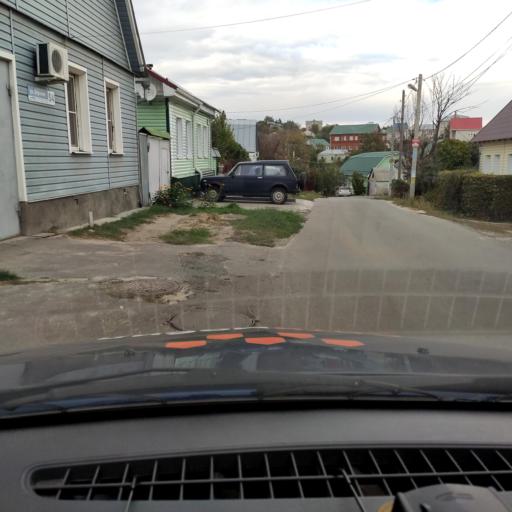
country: RU
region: Voronezj
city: Voronezh
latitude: 51.6285
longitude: 39.1974
